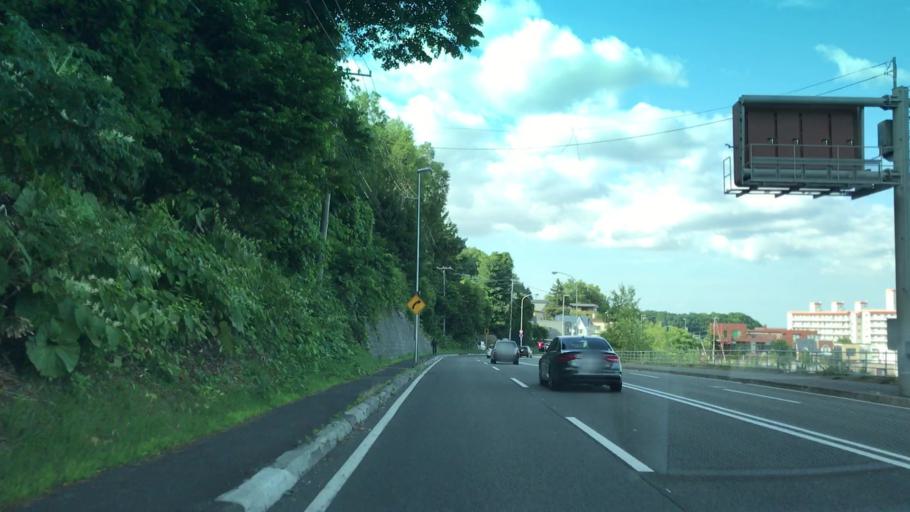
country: JP
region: Hokkaido
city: Sapporo
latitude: 42.9799
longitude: 141.3462
